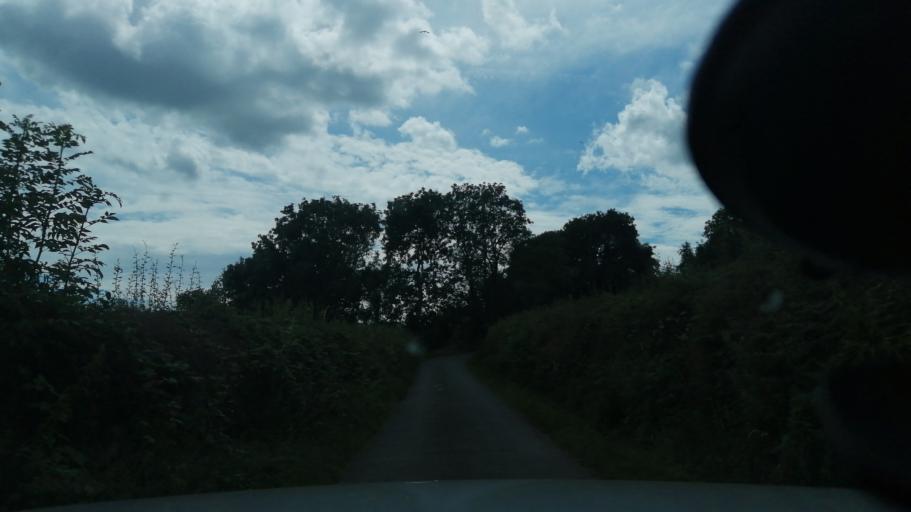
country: GB
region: England
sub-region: Herefordshire
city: Thruxton
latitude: 52.0137
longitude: -2.8072
